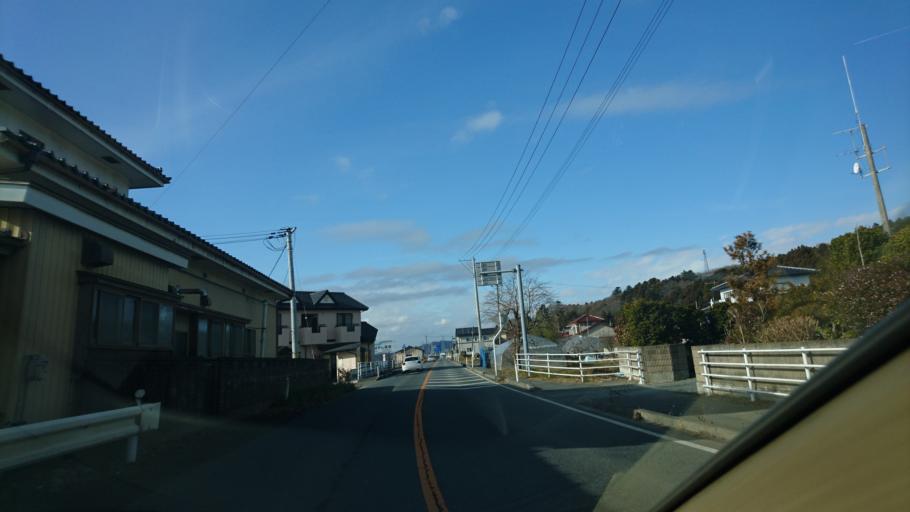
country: JP
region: Miyagi
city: Yamoto
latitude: 38.4571
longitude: 141.2506
